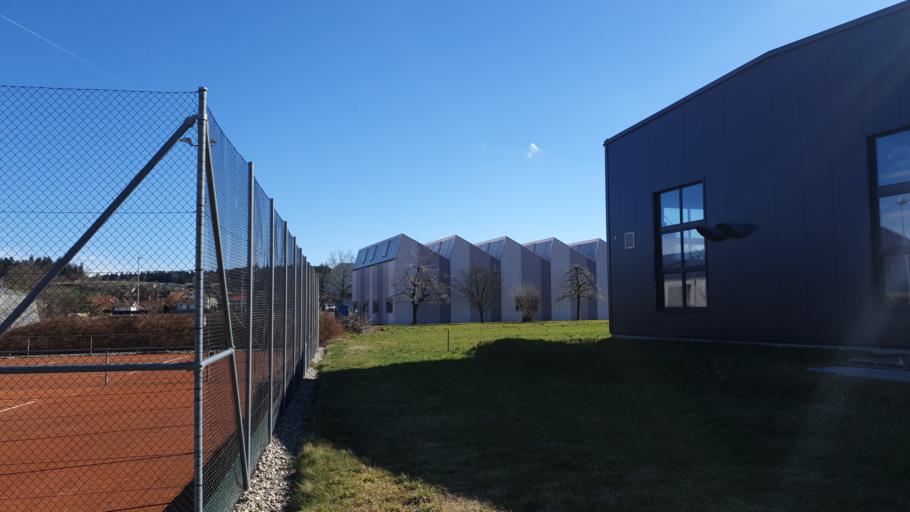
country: CH
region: Bern
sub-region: Oberaargau
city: Lotzwil
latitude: 47.1925
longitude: 7.7850
